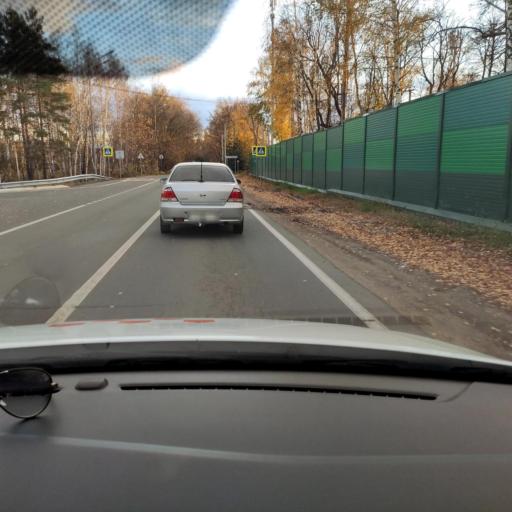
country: RU
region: Tatarstan
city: Verkhniy Uslon
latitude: 55.6255
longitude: 49.0139
